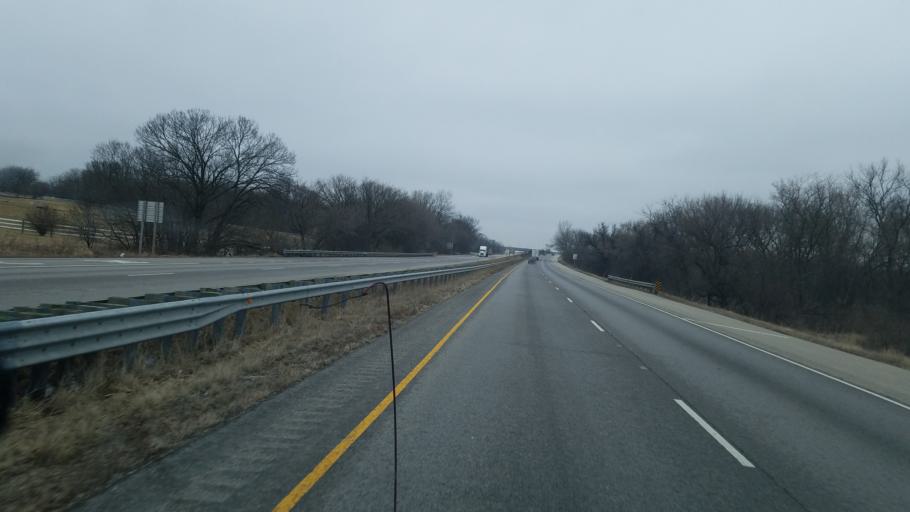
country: US
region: Illinois
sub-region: Lake County
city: Wadsworth
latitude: 42.4704
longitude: -87.9468
